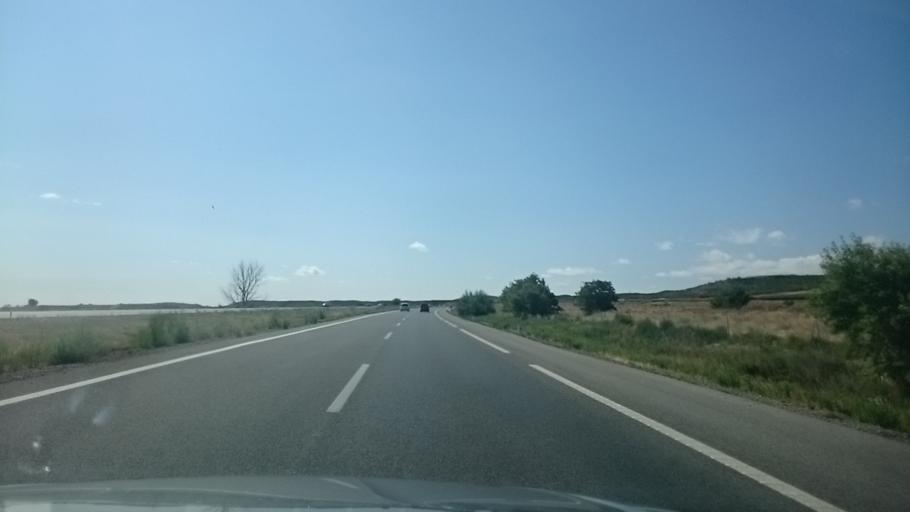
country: ES
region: Navarre
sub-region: Provincia de Navarra
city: Ribaforada
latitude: 41.9536
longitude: -1.5352
